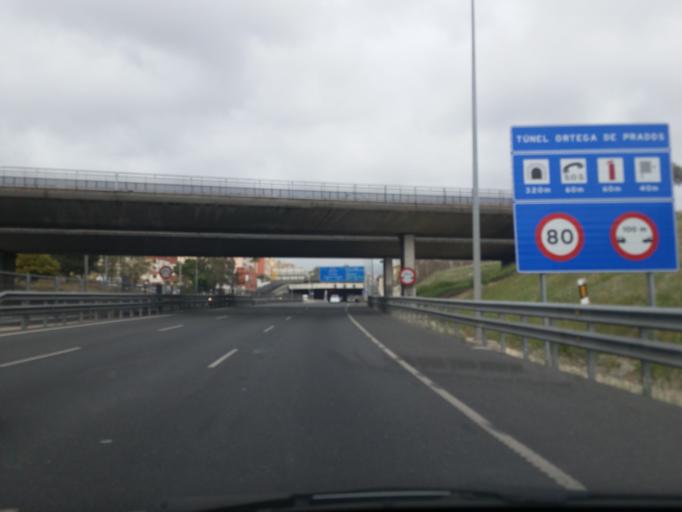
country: ES
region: Andalusia
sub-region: Provincia de Malaga
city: Malaga
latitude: 36.7192
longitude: -4.4575
